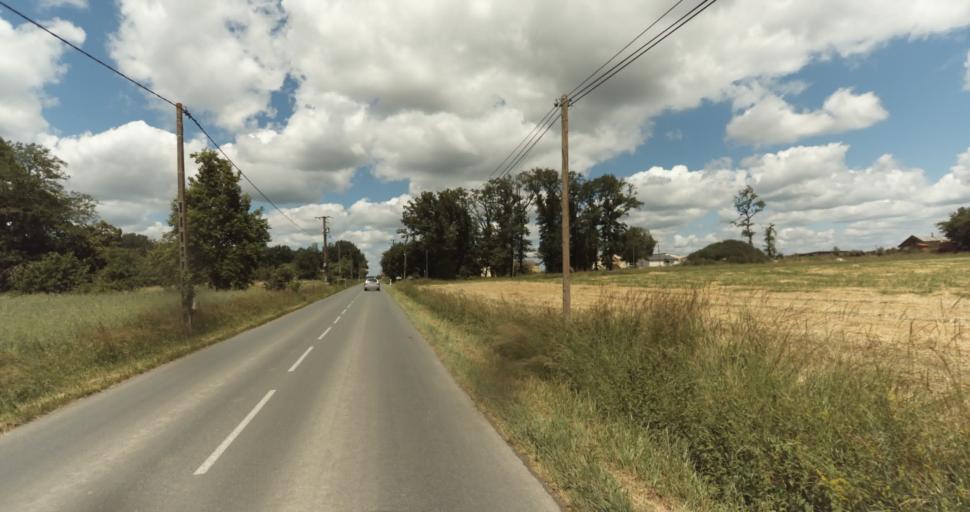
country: FR
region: Aquitaine
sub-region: Departement de la Dordogne
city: Beaumont-du-Perigord
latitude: 44.7308
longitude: 0.7558
